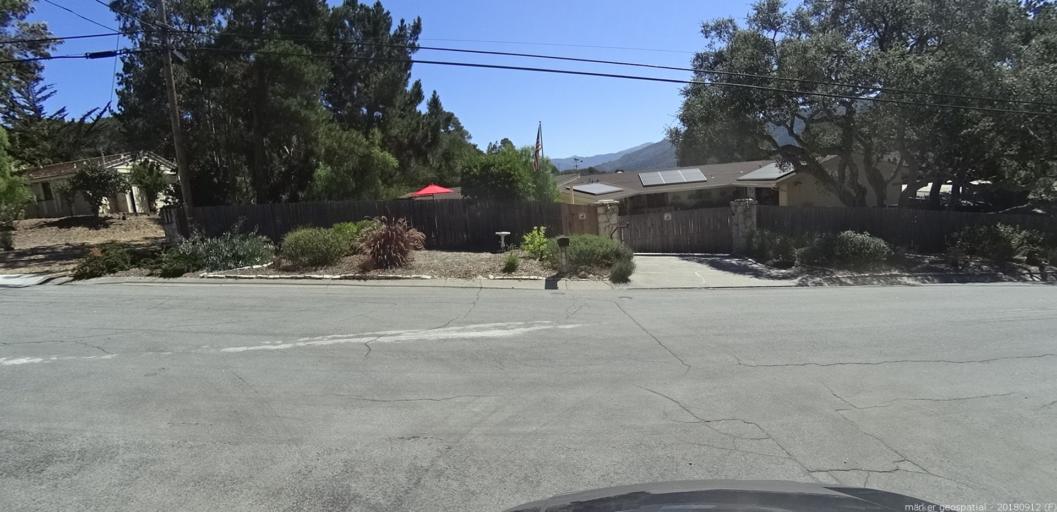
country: US
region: California
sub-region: Monterey County
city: Carmel Valley Village
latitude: 36.4922
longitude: -121.7391
